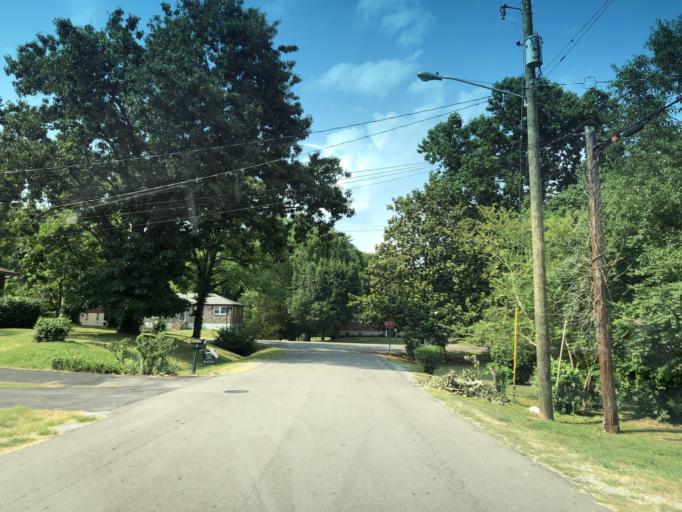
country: US
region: Tennessee
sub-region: Davidson County
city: Goodlettsville
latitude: 36.2554
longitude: -86.7267
